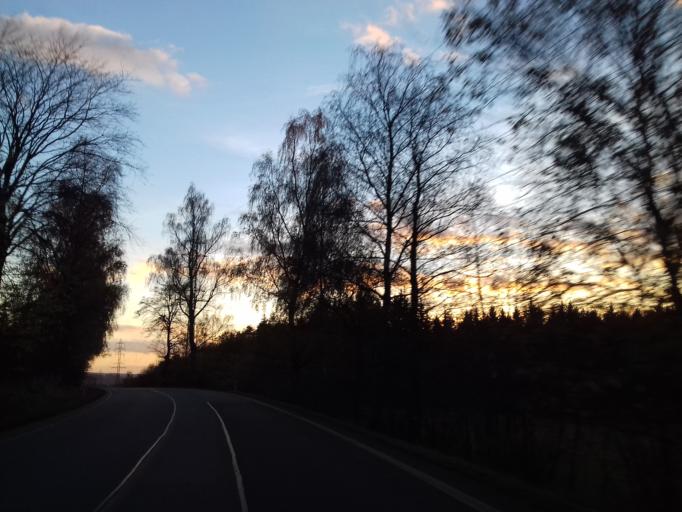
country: CZ
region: Pardubicky
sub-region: Okres Chrudim
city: Hlinsko
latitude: 49.7385
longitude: 15.8788
